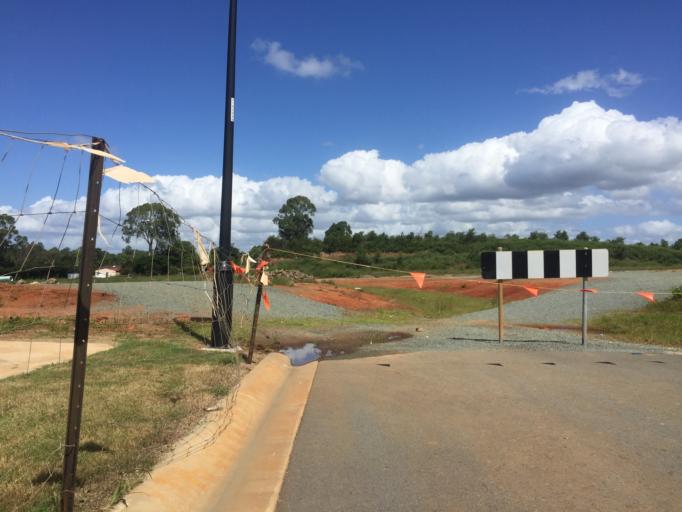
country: AU
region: Queensland
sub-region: Moreton Bay
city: Morayfield
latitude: -27.1118
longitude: 152.9288
